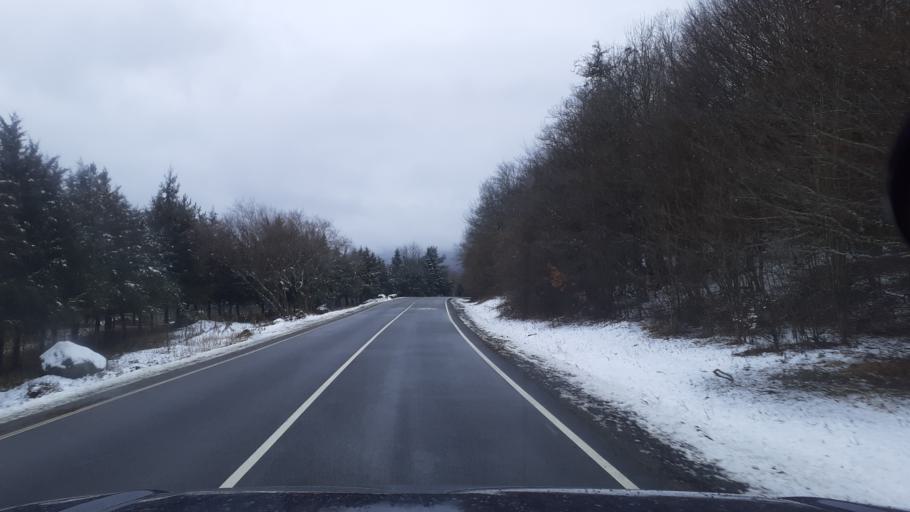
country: RU
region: Adygeya
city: Kamennomostskiy
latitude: 44.1161
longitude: 40.1207
